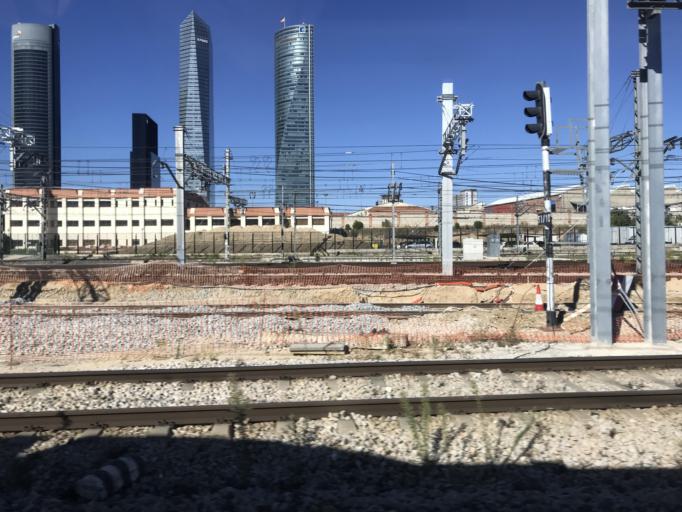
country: ES
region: Madrid
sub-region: Provincia de Madrid
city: Pinar de Chamartin
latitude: 40.4782
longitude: -3.6797
